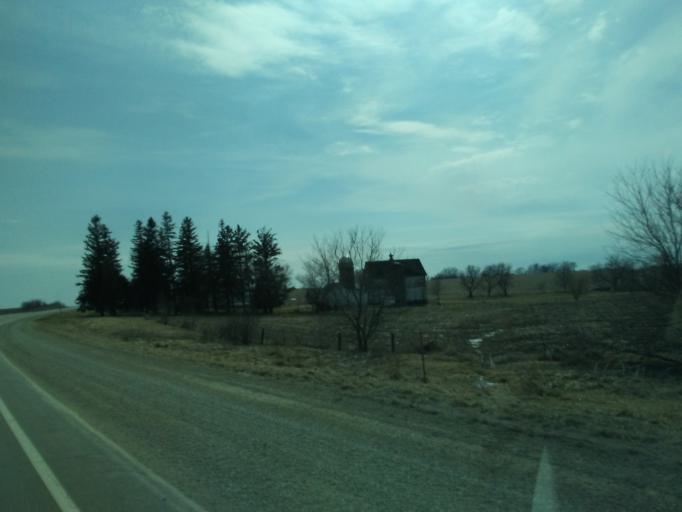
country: US
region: Iowa
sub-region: Winneshiek County
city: Decorah
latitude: 43.4487
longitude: -91.8632
